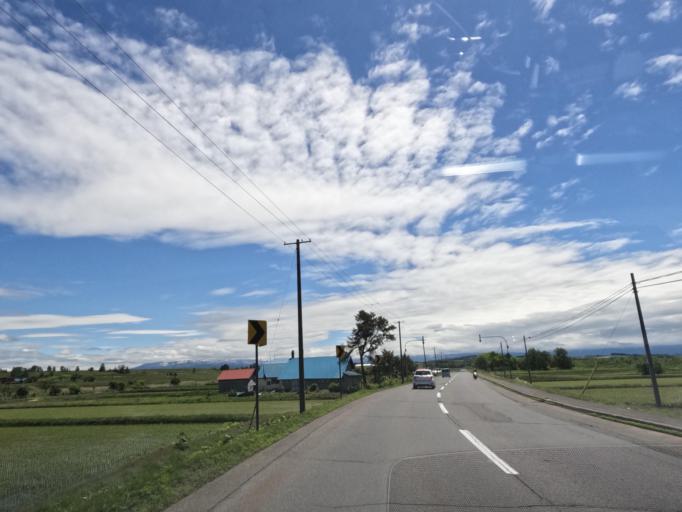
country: JP
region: Hokkaido
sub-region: Asahikawa-shi
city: Asahikawa
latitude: 43.6650
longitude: 142.4220
